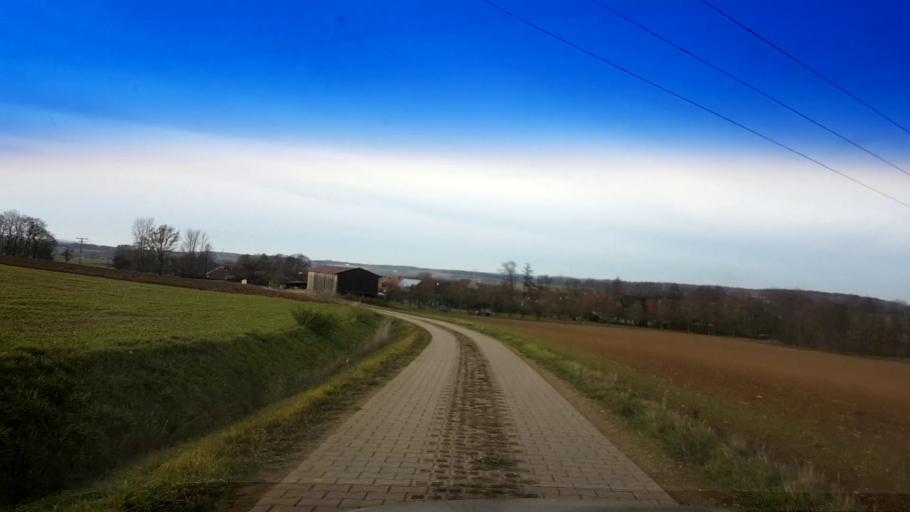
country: DE
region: Bavaria
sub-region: Upper Franconia
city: Schesslitz
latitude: 49.9536
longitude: 11.0252
